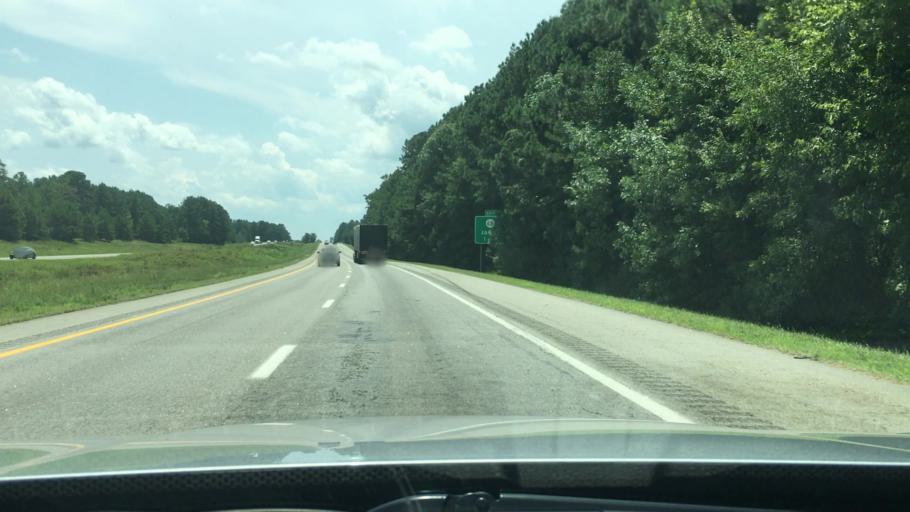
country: US
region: Virginia
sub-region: City of Emporia
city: Emporia
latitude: 36.8235
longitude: -77.4546
